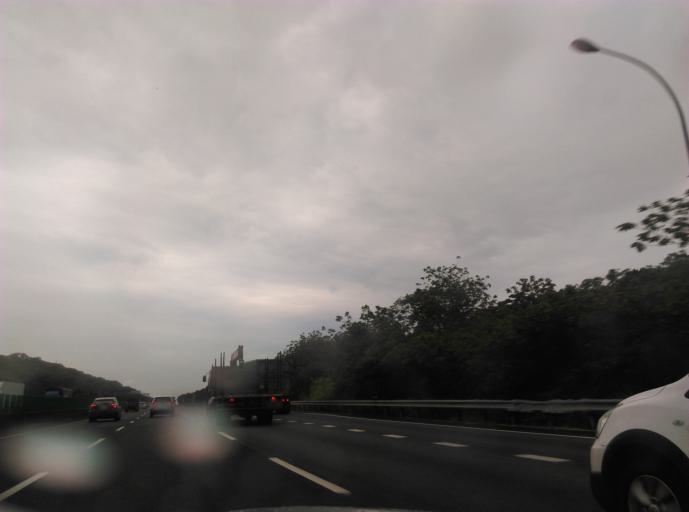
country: TW
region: Taiwan
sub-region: Hsinchu
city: Hsinchu
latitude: 24.7270
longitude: 120.9021
